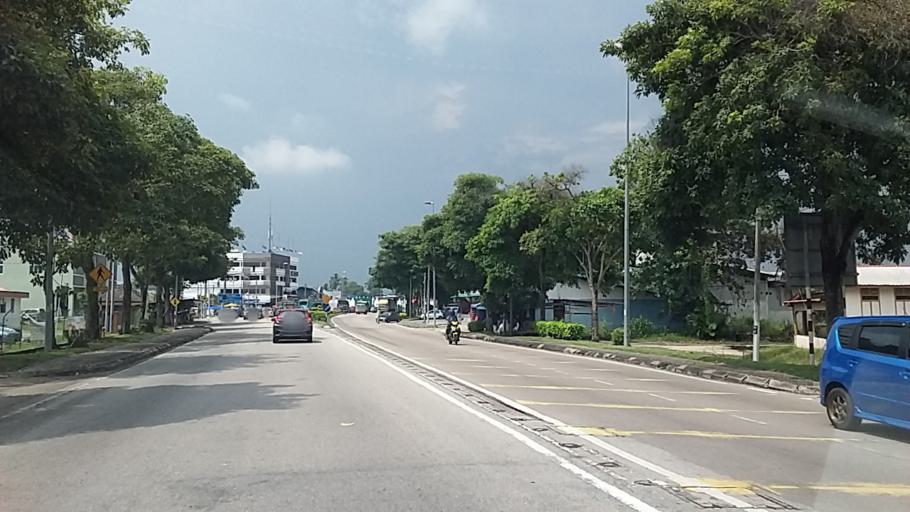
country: MY
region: Johor
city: Parit Raja
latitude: 1.8643
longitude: 103.1098
